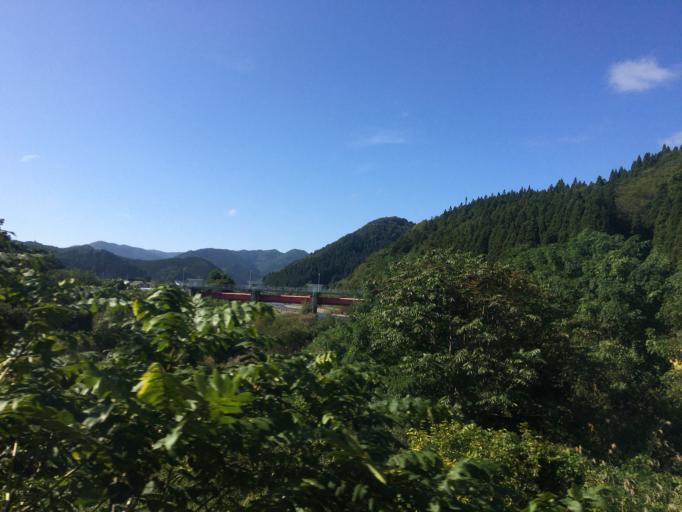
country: JP
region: Aomori
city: Hirosaki
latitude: 40.5264
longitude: 140.5508
